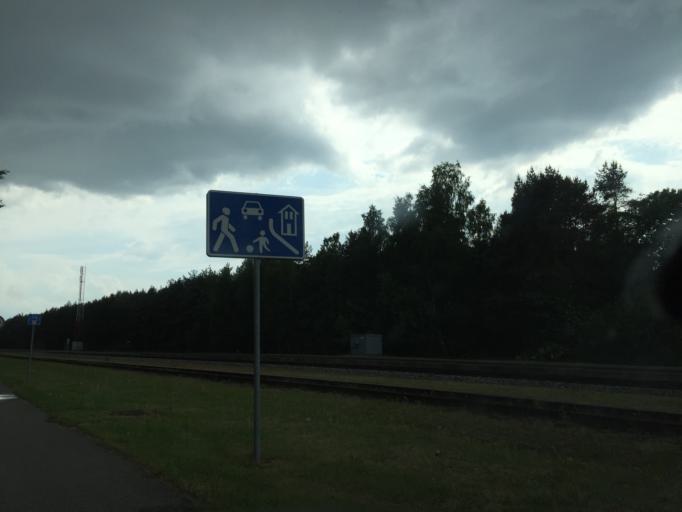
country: LT
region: Klaipedos apskritis
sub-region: Klaipeda
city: Klaipeda
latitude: 55.7685
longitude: 21.0958
